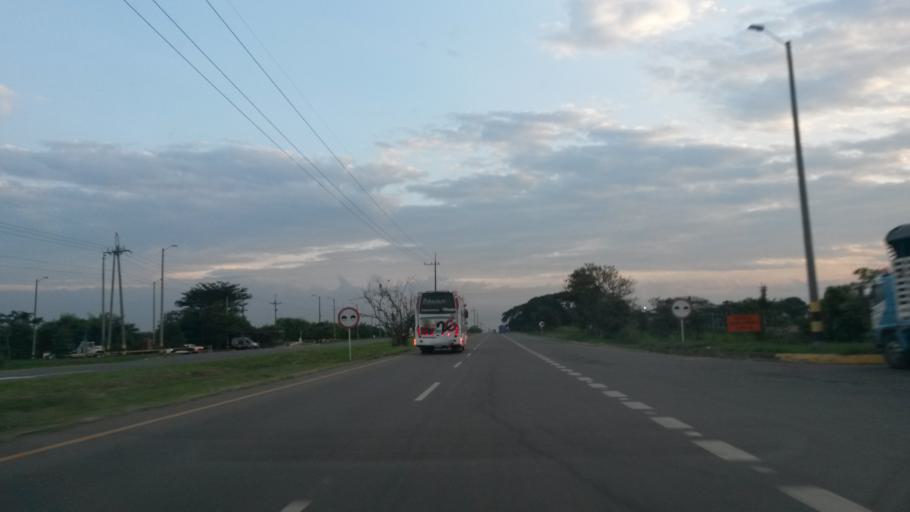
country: CO
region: Cauca
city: Puerto Tejada
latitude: 3.1321
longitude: -76.4634
